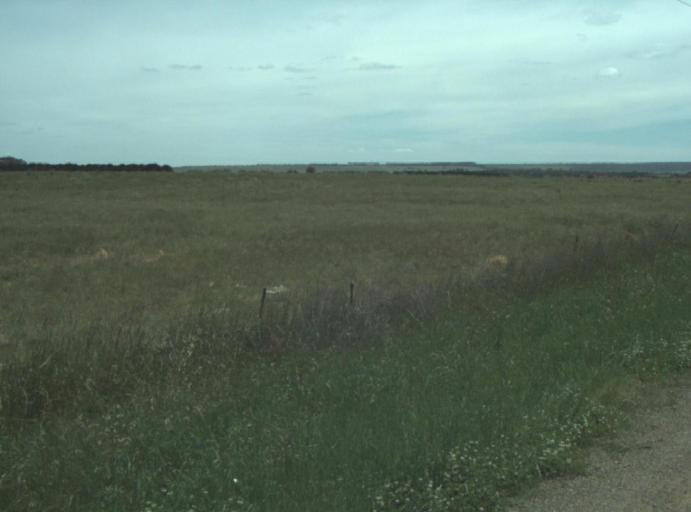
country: AU
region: Victoria
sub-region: Greater Geelong
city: Bell Post Hill
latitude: -38.0083
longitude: 144.2839
